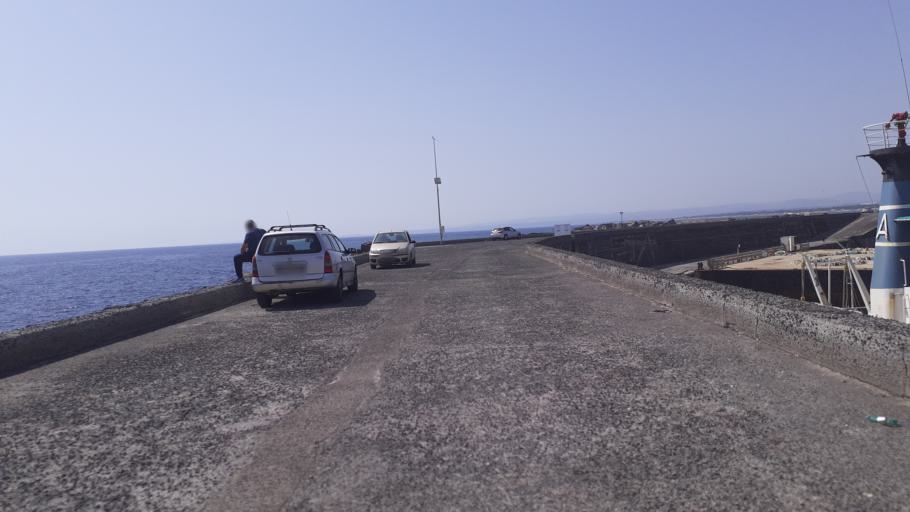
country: IT
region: Sicily
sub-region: Catania
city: Catania
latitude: 37.4888
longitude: 15.1001
